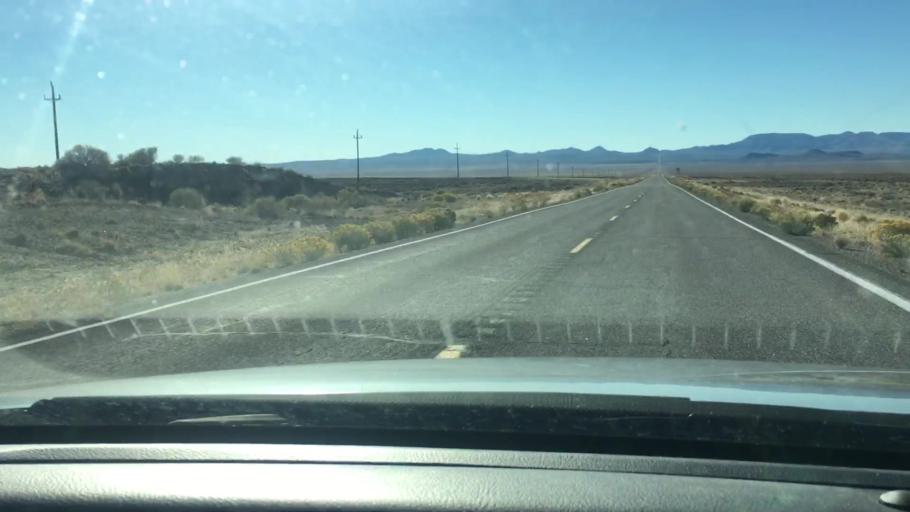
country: US
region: Nevada
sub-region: Nye County
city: Tonopah
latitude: 38.1627
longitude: -116.4785
